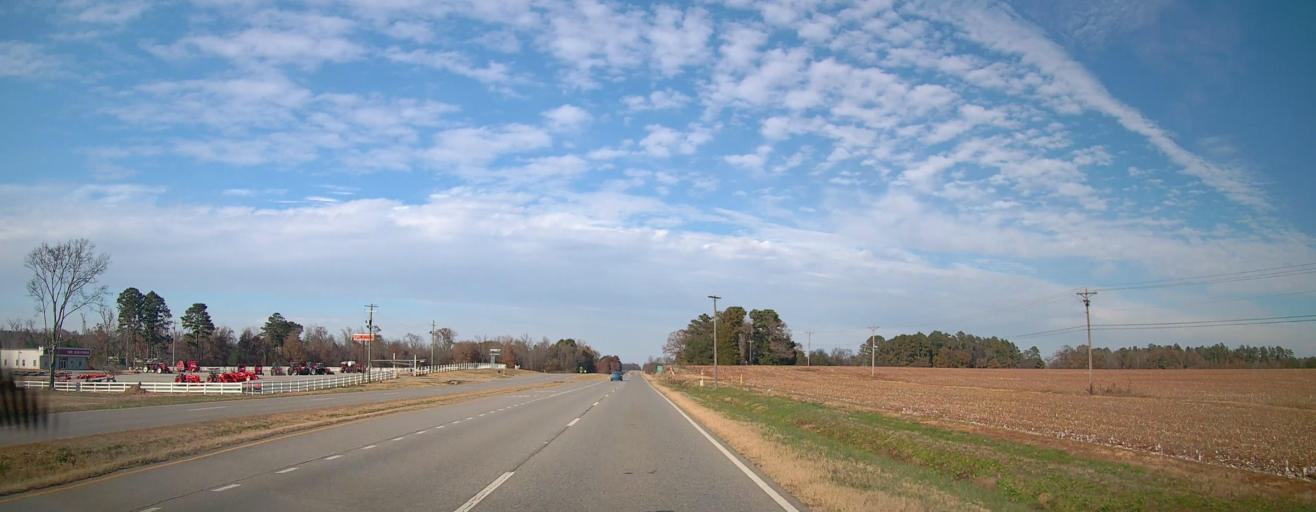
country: US
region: Alabama
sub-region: Morgan County
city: Decatur
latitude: 34.6687
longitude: -86.9500
